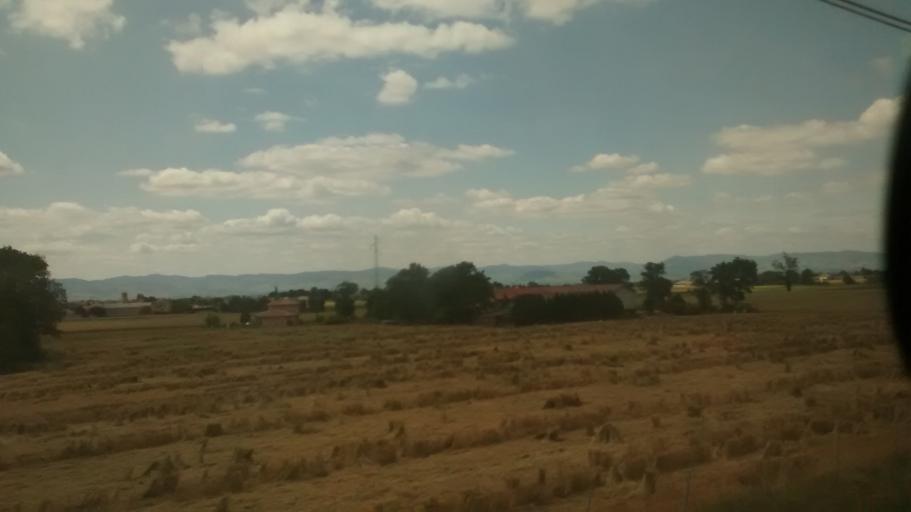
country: FR
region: Rhone-Alpes
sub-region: Departement de l'Ain
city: Villeneuve
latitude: 46.0199
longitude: 4.8535
